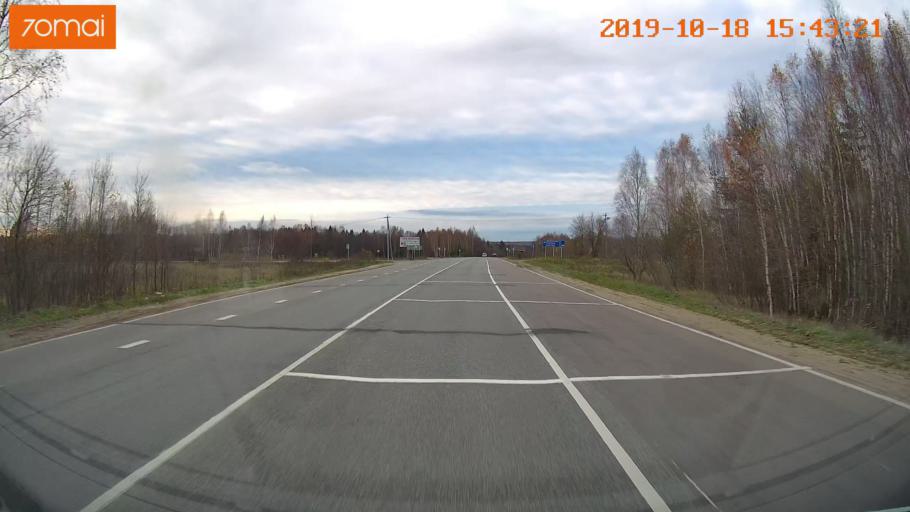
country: RU
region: Vladimir
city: Golovino
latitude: 55.9663
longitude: 40.5525
